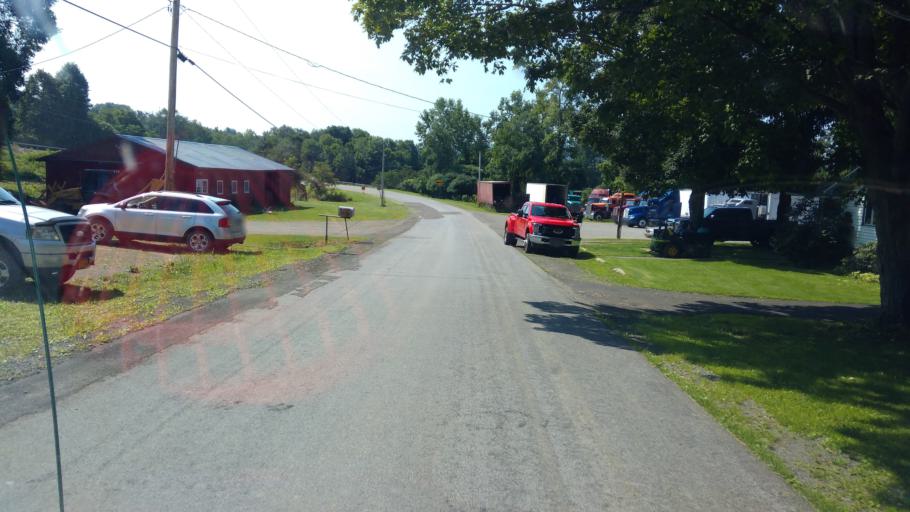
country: US
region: New York
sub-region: Allegany County
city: Belmont
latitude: 42.2420
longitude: -78.0156
